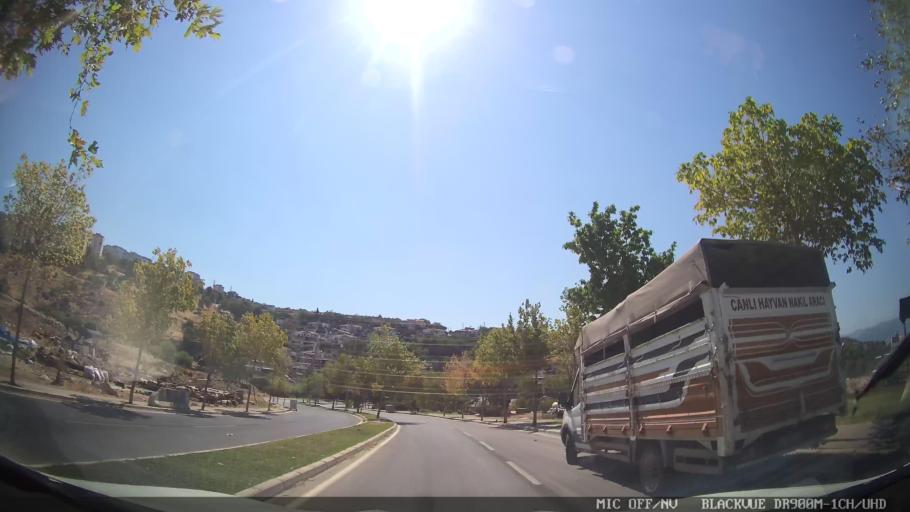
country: TR
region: Izmir
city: Karsiyaka
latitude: 38.5037
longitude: 27.0826
